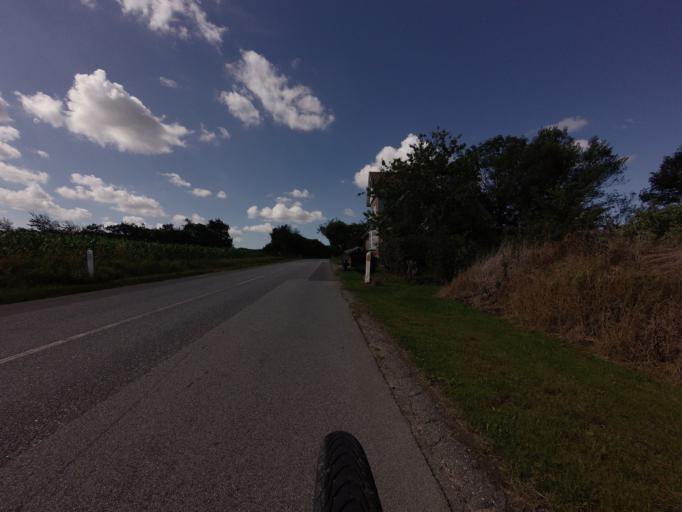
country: DK
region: North Denmark
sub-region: Hjorring Kommune
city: Hjorring
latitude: 57.4792
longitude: 9.9122
